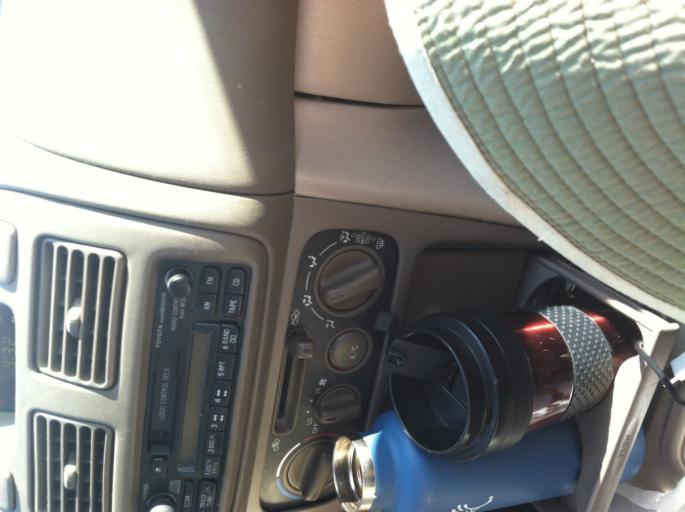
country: US
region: Massachusetts
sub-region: Suffolk County
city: Revere
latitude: 42.4040
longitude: -70.9908
